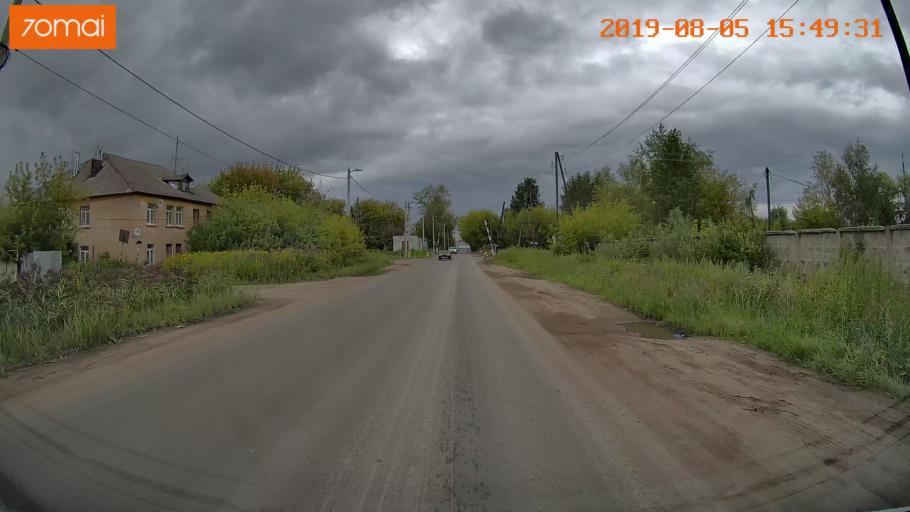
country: RU
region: Ivanovo
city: Novo-Talitsy
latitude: 56.9949
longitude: 40.9124
